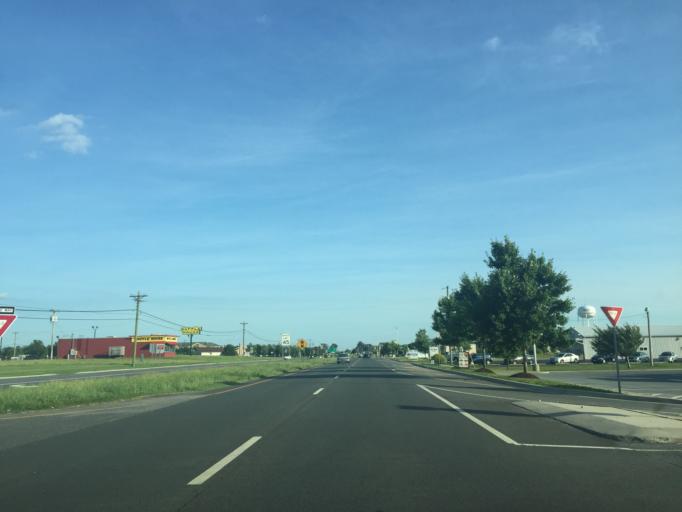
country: US
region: Delaware
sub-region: Kent County
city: Smyrna
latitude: 39.2857
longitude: -75.5946
